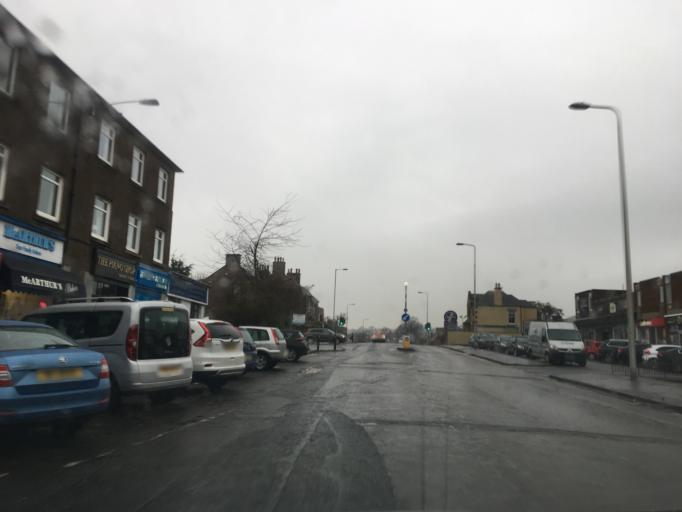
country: GB
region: Scotland
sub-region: Edinburgh
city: Colinton
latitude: 55.9359
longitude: -3.2789
